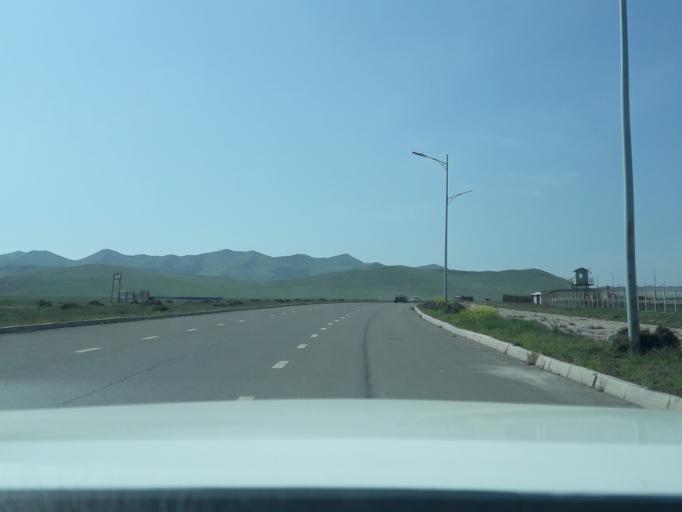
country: MN
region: Ulaanbaatar
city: Ulaanbaatar
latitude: 47.8310
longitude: 106.7863
